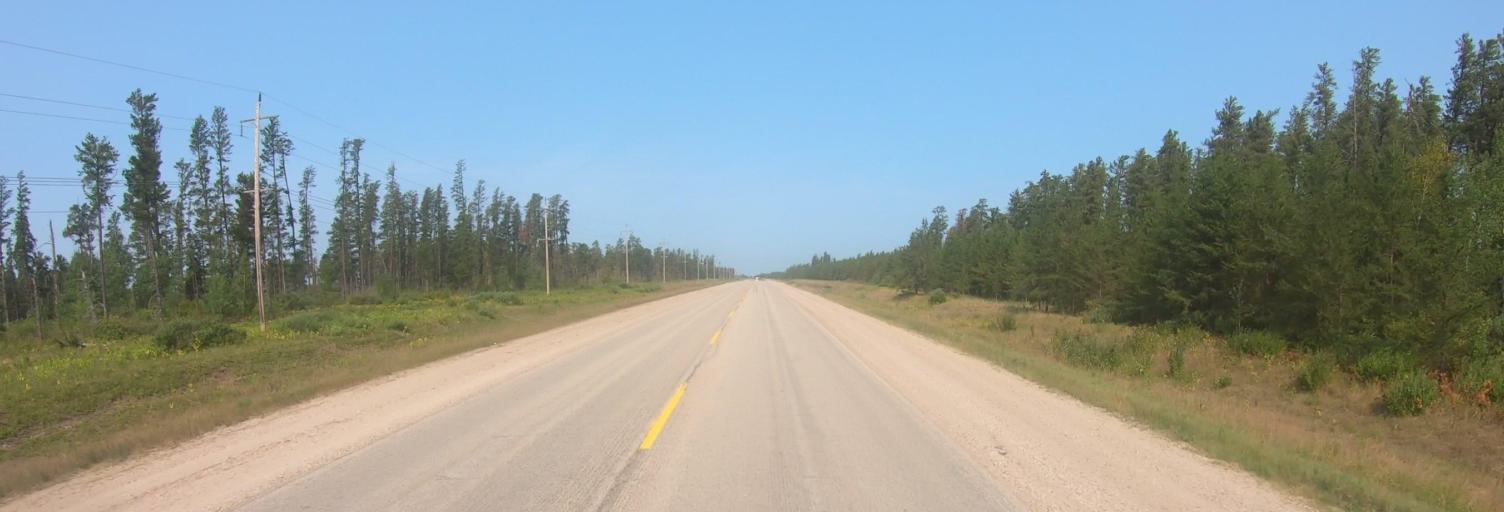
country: US
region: Minnesota
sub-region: Roseau County
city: Roseau
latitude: 49.0822
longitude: -95.8744
